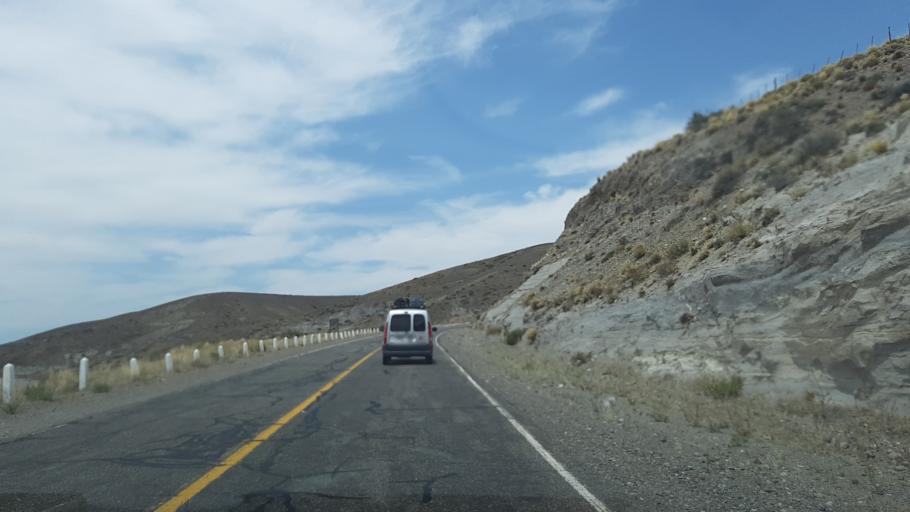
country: AR
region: Rio Negro
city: Pilcaniyeu
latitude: -40.4650
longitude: -70.6582
